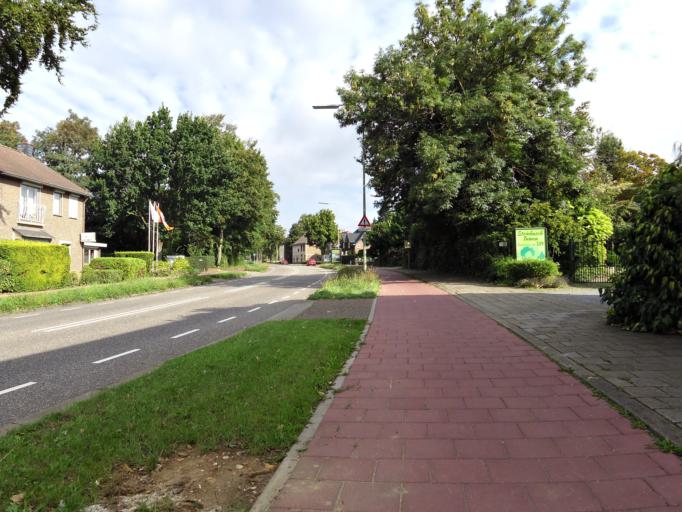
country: NL
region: Limburg
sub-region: Gemeente Kerkrade
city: Kerkrade
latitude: 50.9051
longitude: 6.0582
